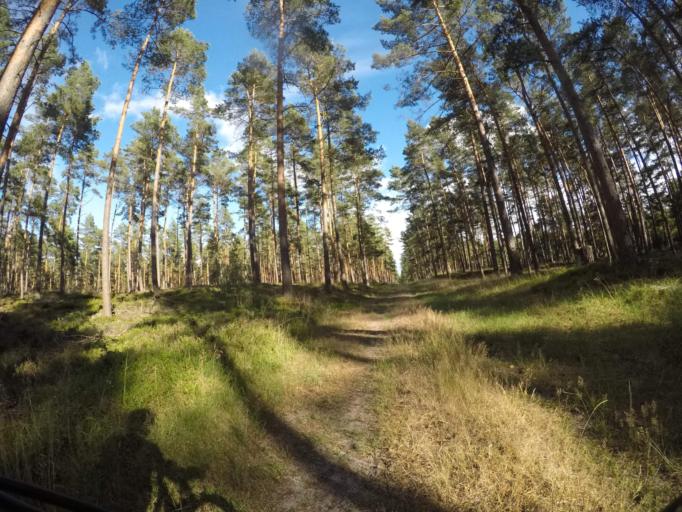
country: DE
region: Mecklenburg-Vorpommern
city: Lubtheen
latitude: 53.2527
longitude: 11.0016
